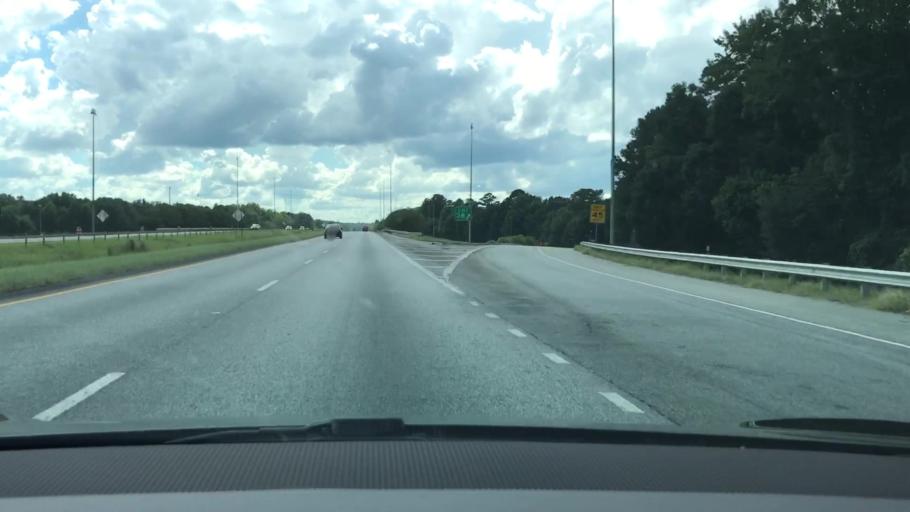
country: US
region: Alabama
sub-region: Macon County
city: Tuskegee
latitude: 32.4731
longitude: -85.6893
